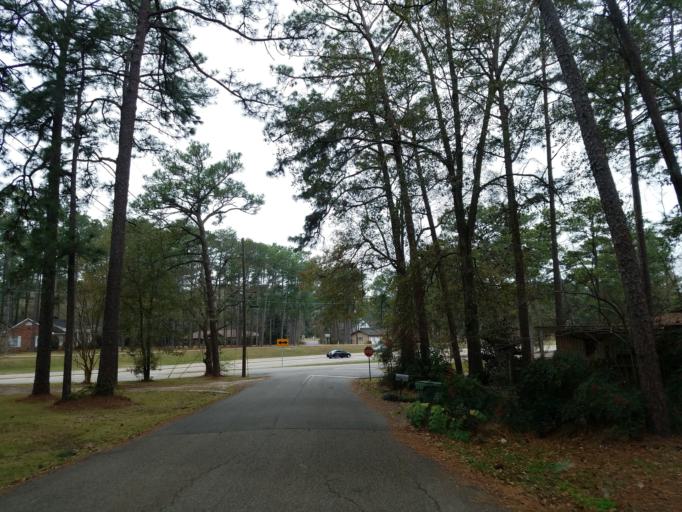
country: US
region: Mississippi
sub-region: Forrest County
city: Hattiesburg
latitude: 31.3137
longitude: -89.3222
